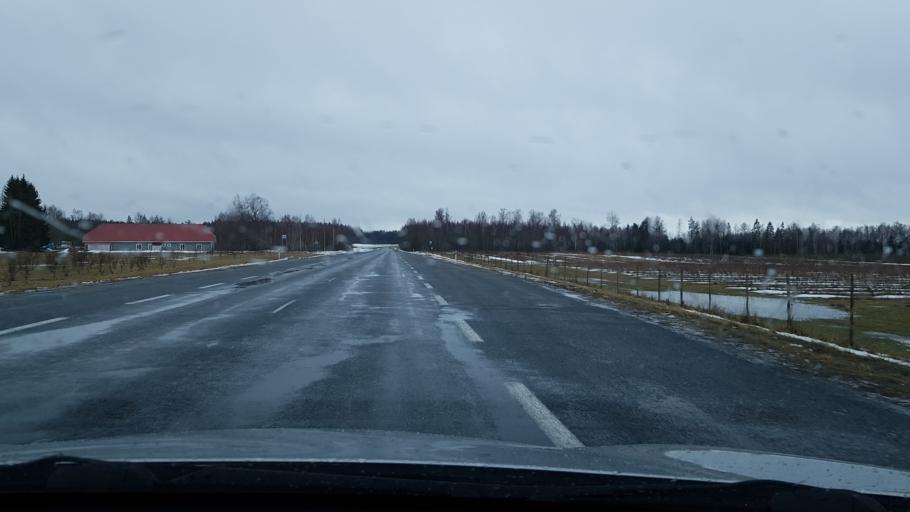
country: LV
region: Apes Novads
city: Ape
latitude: 57.6813
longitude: 26.7249
